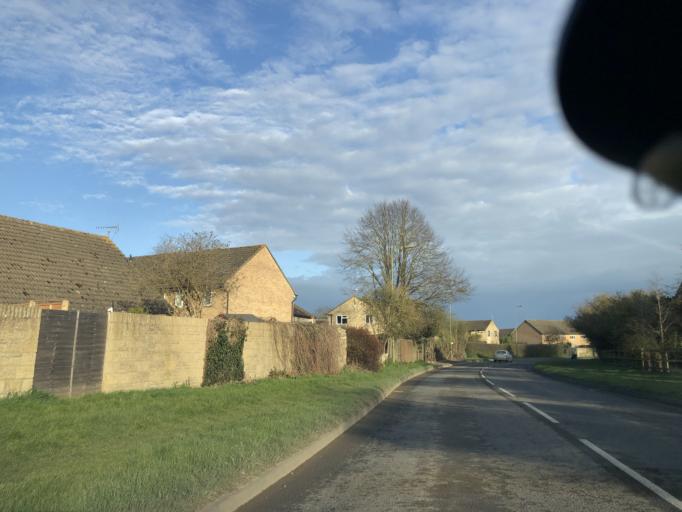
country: GB
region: England
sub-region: Oxfordshire
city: Witney
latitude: 51.7787
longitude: -1.5088
